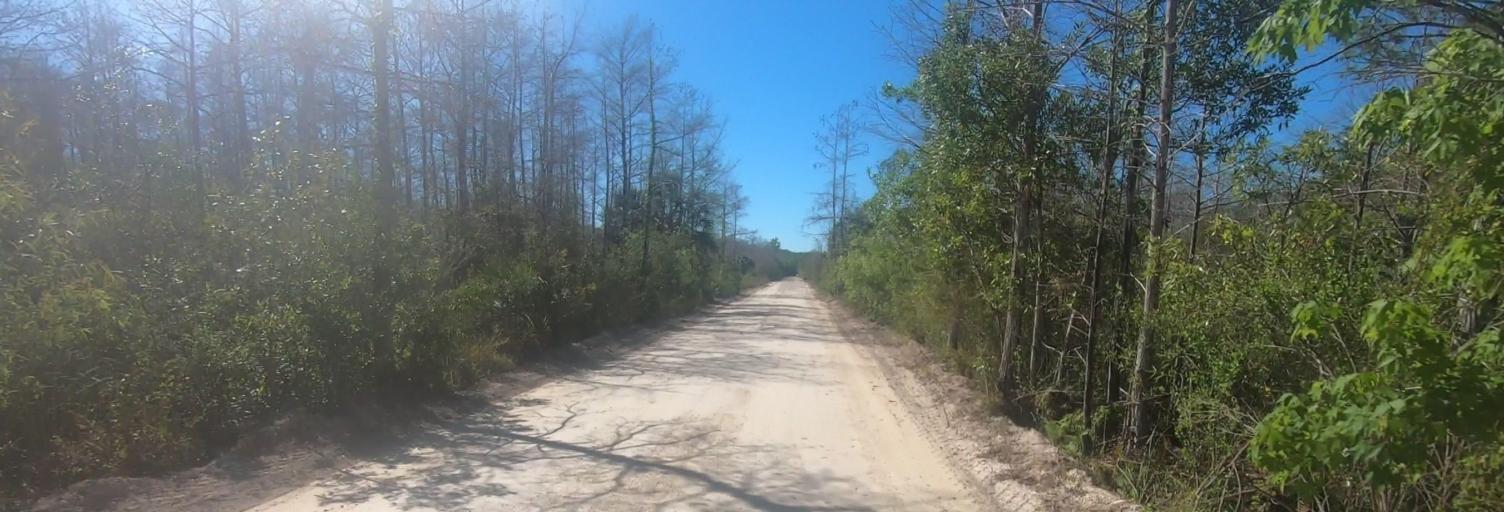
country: US
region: Florida
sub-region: Collier County
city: Marco
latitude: 25.8833
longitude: -81.2298
